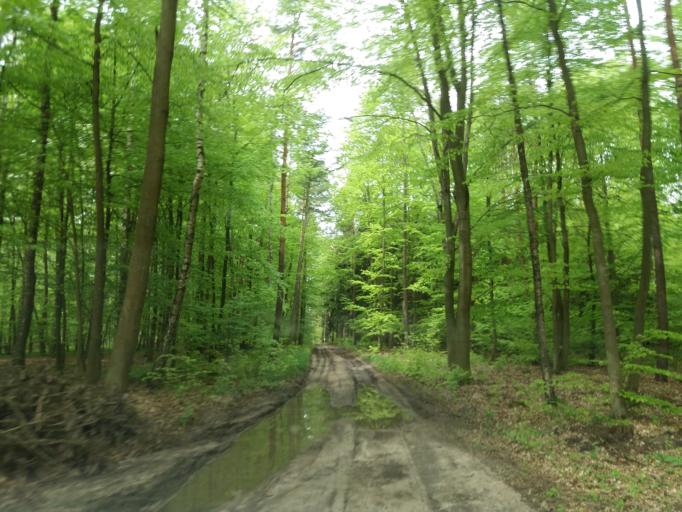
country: PL
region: West Pomeranian Voivodeship
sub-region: Powiat choszczenski
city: Bierzwnik
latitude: 53.0735
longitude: 15.6680
